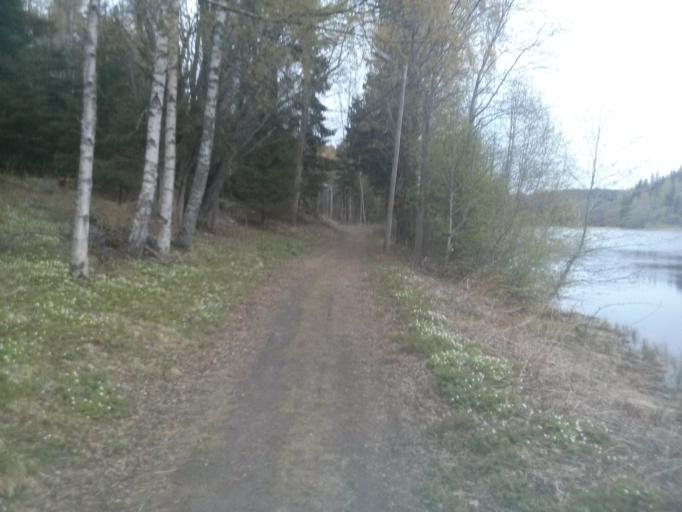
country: SE
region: Vaesternorrland
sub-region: Sundsvalls Kommun
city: Nolby
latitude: 62.2975
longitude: 17.3564
